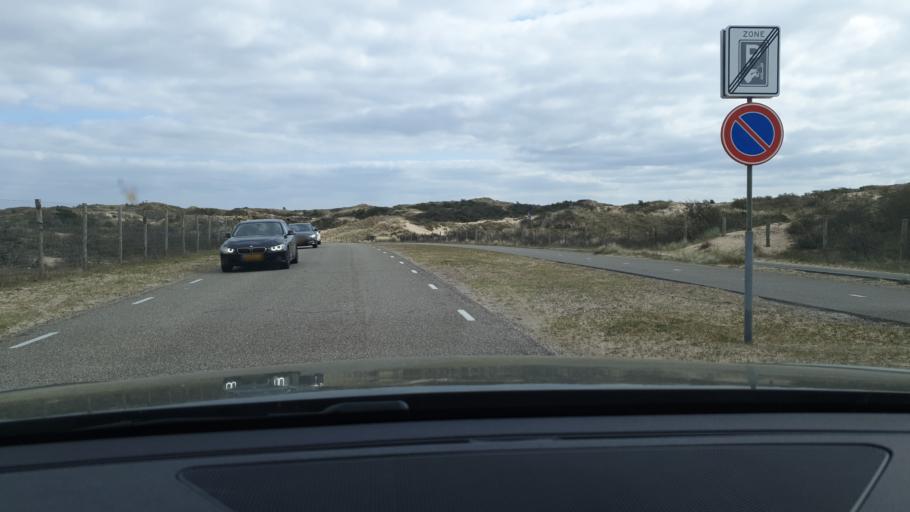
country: NL
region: South Holland
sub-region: Gemeente Noordwijkerhout
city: Noordwijkerhout
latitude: 52.2963
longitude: 4.4810
